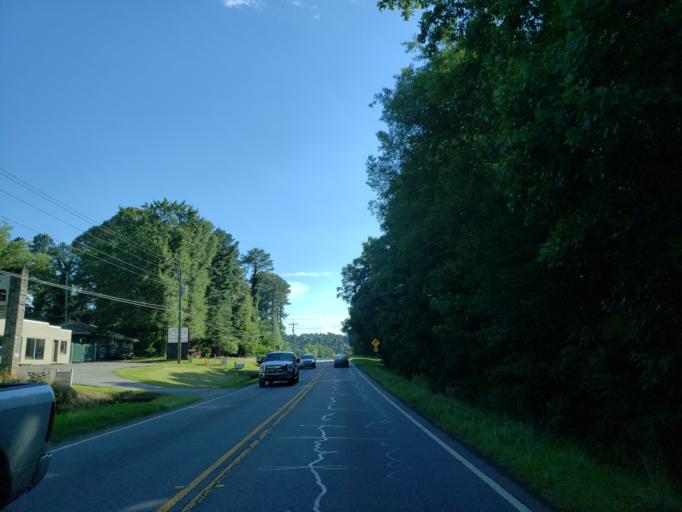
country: US
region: Georgia
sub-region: Fulton County
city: Milton
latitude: 34.2326
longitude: -84.2689
